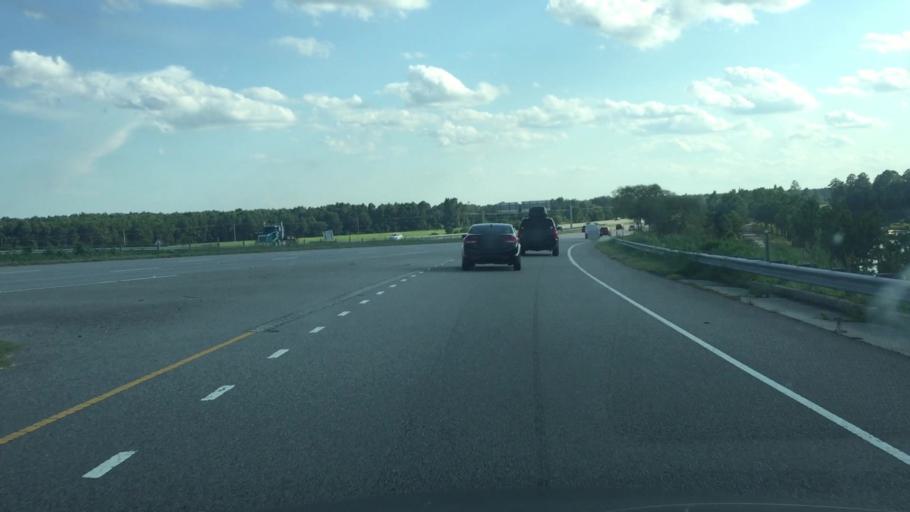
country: US
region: South Carolina
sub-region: Horry County
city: North Myrtle Beach
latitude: 33.8423
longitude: -78.7029
